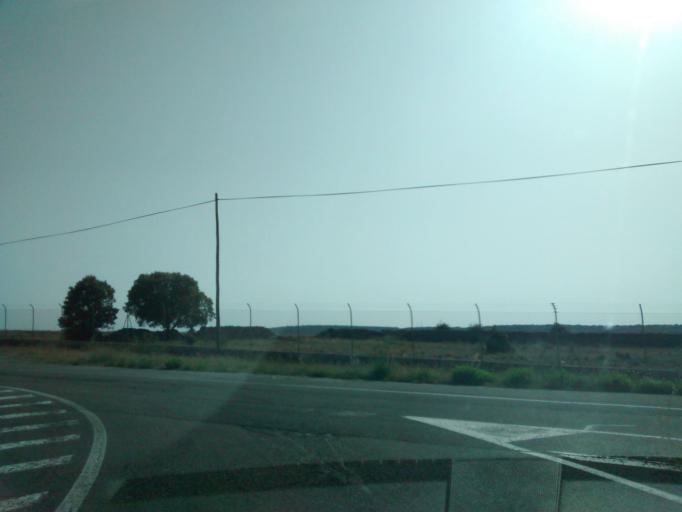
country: ES
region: Castille-La Mancha
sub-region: Provincia de Guadalajara
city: Sauca
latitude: 41.0263
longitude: -2.5204
